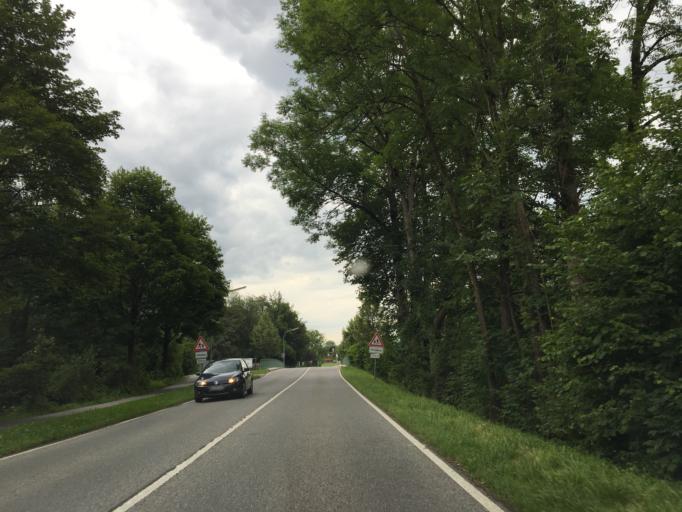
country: DE
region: Bavaria
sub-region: Upper Bavaria
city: Oberaudorf
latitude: 47.6601
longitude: 12.1714
